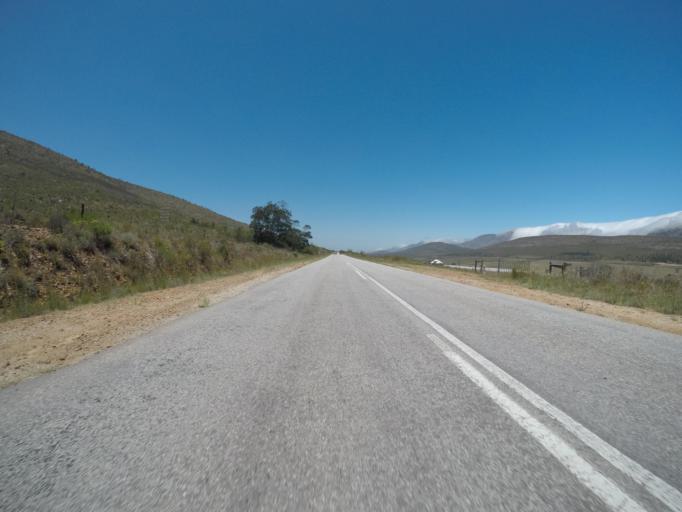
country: ZA
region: Eastern Cape
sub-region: Cacadu District Municipality
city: Kareedouw
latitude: -33.8387
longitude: 23.9259
